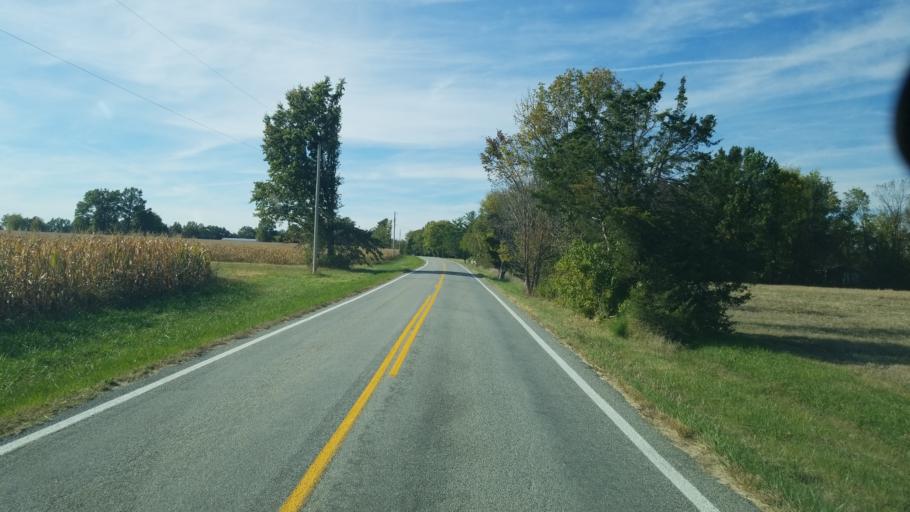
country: US
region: Ohio
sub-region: Warren County
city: Morrow
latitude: 39.4051
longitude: -84.0521
